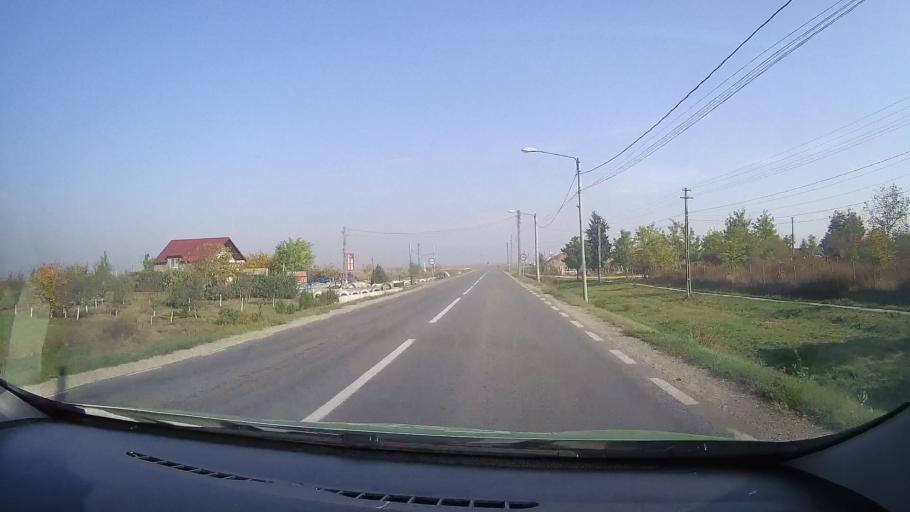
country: RO
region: Arad
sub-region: Comuna Pilu
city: Pilu
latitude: 46.5819
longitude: 21.3436
